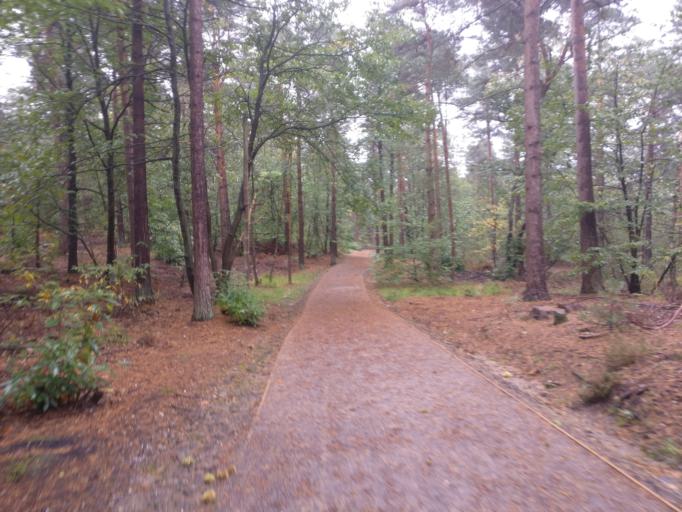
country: GB
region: England
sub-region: Surrey
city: Frimley
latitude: 51.3162
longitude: -0.7083
